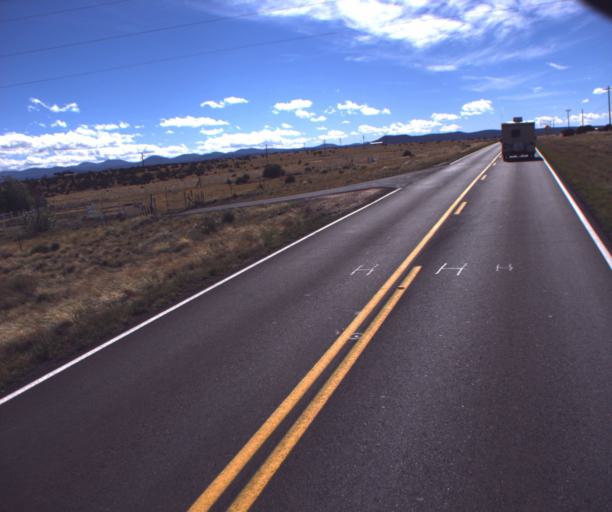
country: US
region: Arizona
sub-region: Navajo County
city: White Mountain Lake
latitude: 34.3754
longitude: -109.6884
